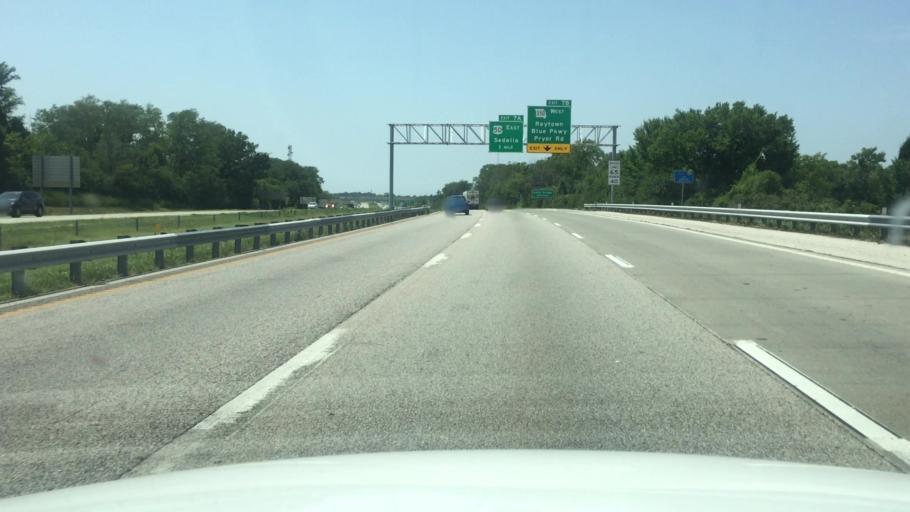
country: US
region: Missouri
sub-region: Jackson County
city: Lees Summit
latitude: 38.9423
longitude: -94.3878
